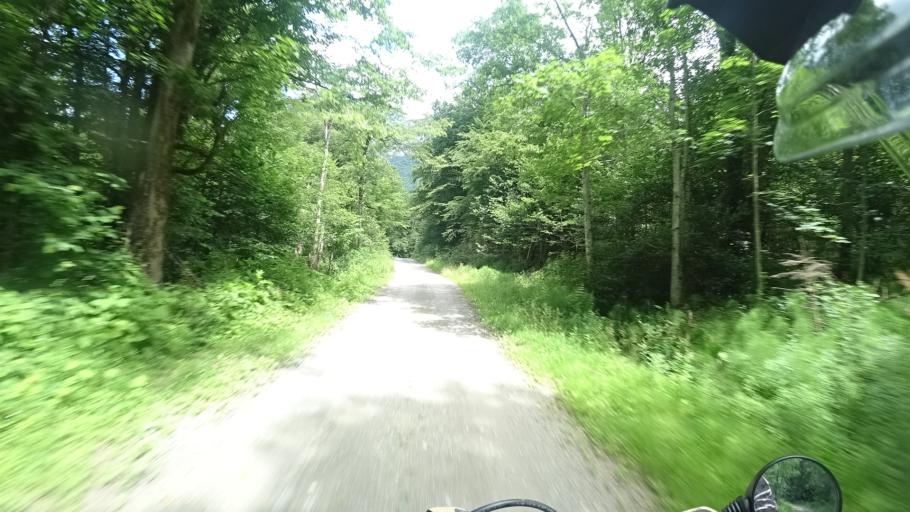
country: SI
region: Osilnica
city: Osilnica
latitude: 45.5245
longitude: 14.7309
